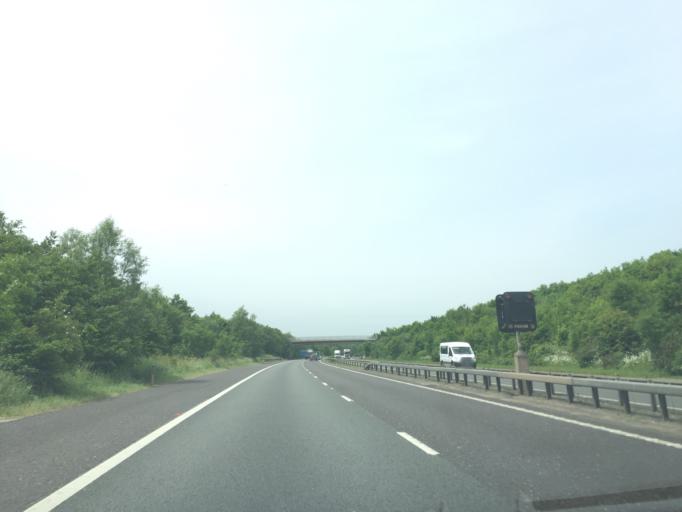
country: GB
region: England
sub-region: Kent
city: Borough Green
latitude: 51.3005
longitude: 0.3202
